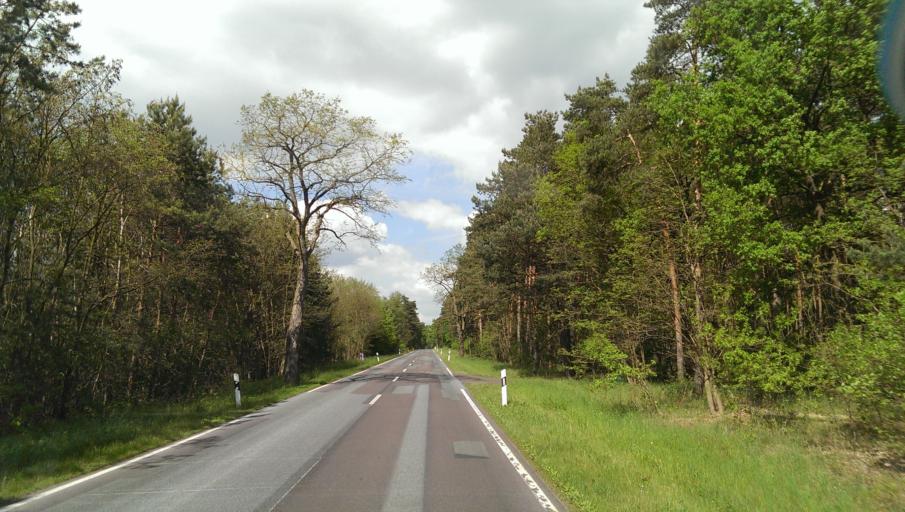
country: DE
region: Saxony-Anhalt
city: Loburg
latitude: 52.1367
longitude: 12.0913
